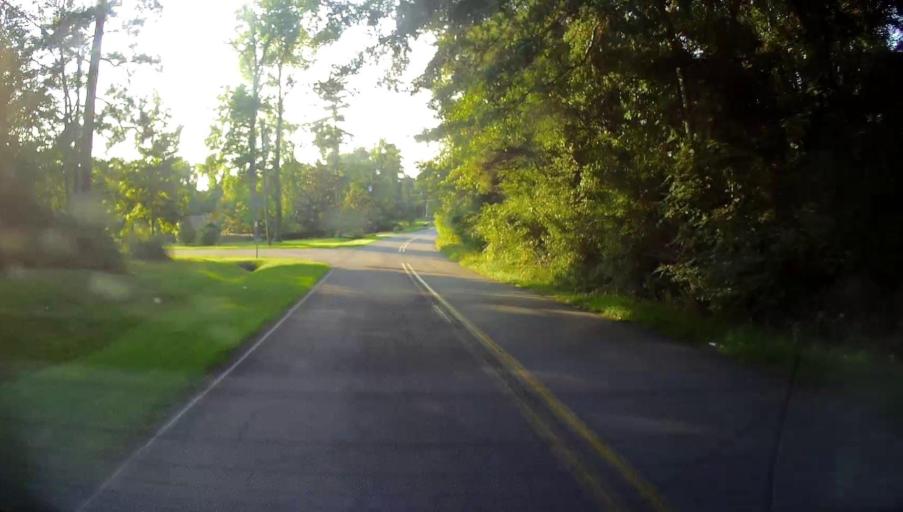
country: US
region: Georgia
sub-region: Bibb County
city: Macon
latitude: 32.8765
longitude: -83.6887
